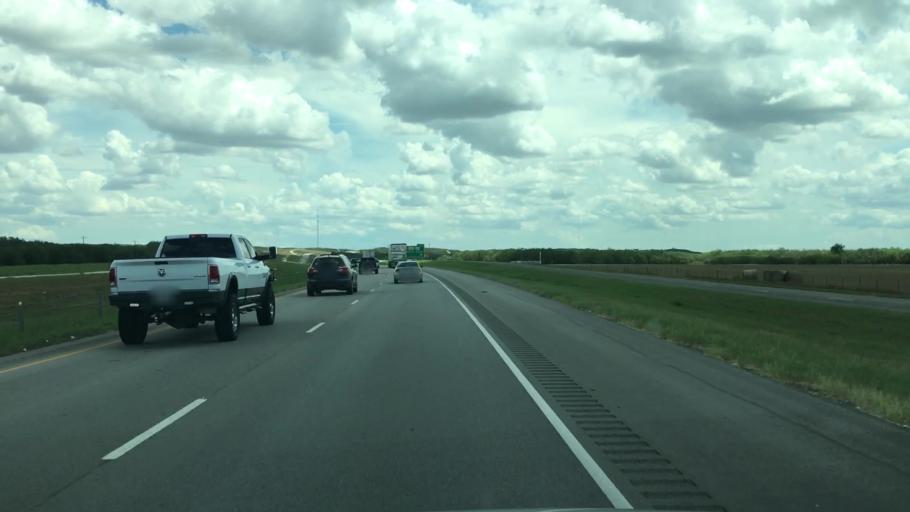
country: US
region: Texas
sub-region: Live Oak County
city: George West
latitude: 28.2687
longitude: -97.9411
